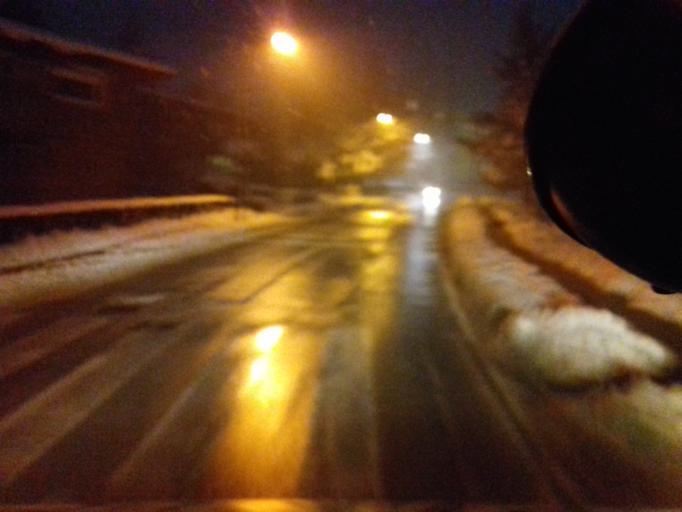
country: BA
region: Federation of Bosnia and Herzegovina
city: Kobilja Glava
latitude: 43.8669
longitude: 18.4195
